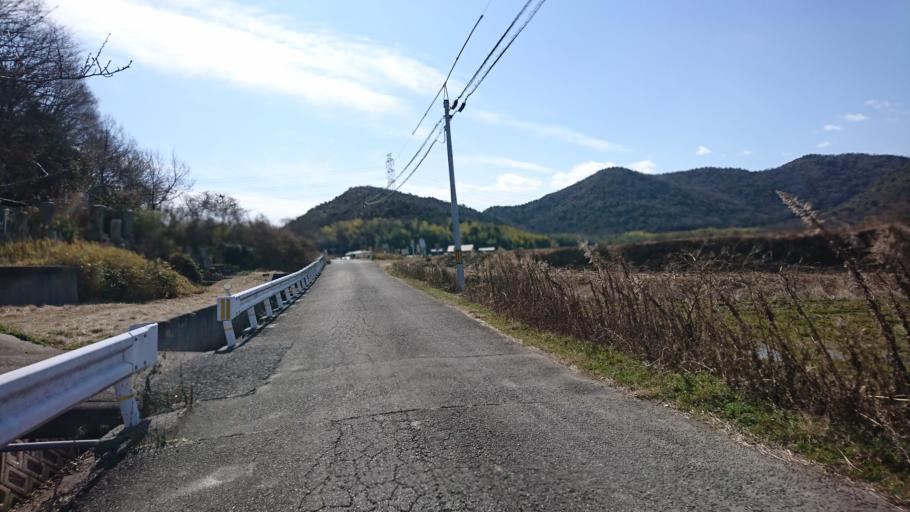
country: JP
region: Hyogo
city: Kakogawacho-honmachi
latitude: 34.8048
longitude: 134.8098
